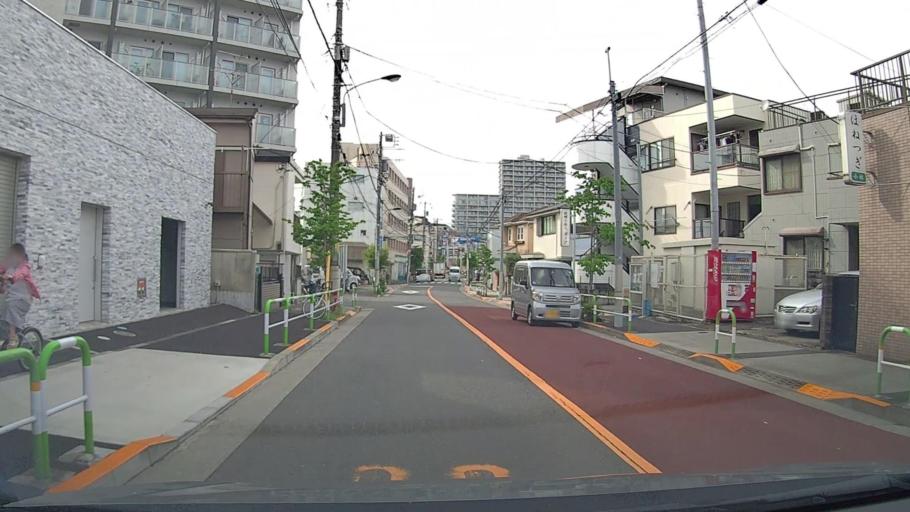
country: JP
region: Saitama
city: Kawaguchi
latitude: 35.7456
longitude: 139.7368
